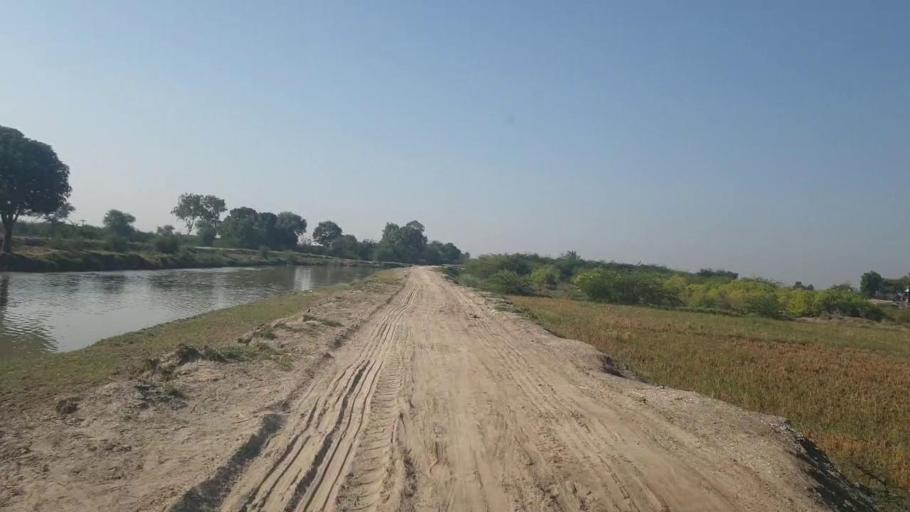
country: PK
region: Sindh
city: Badin
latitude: 24.6808
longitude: 68.8577
